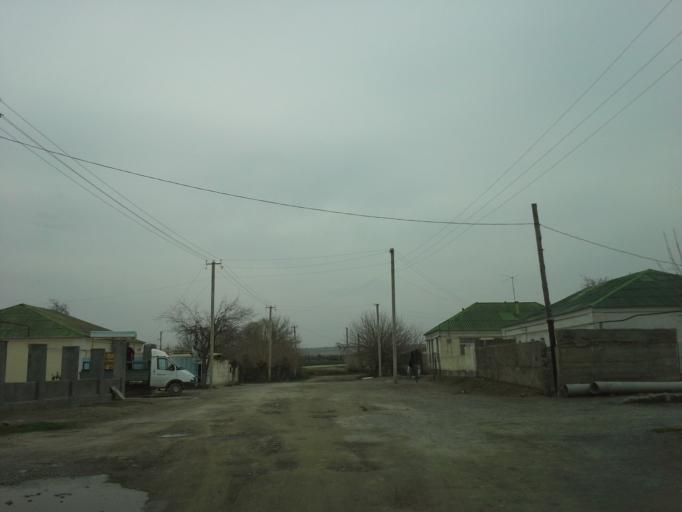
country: TM
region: Ahal
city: Abadan
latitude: 37.9710
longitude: 58.2208
